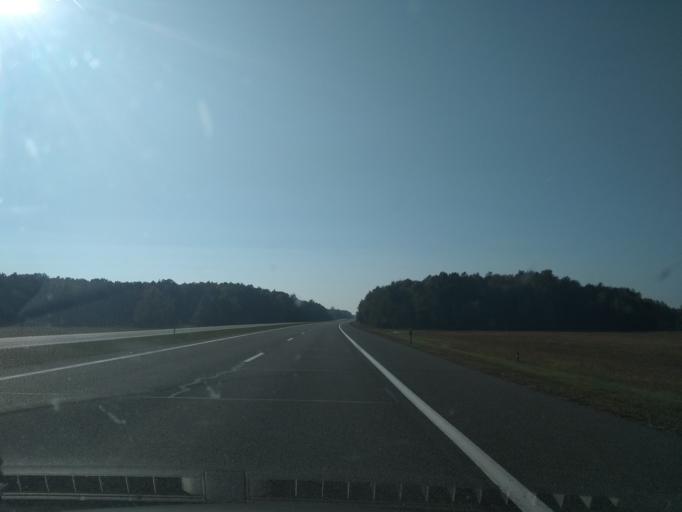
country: BY
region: Brest
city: Horad Kobryn
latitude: 52.2854
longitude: 24.5637
